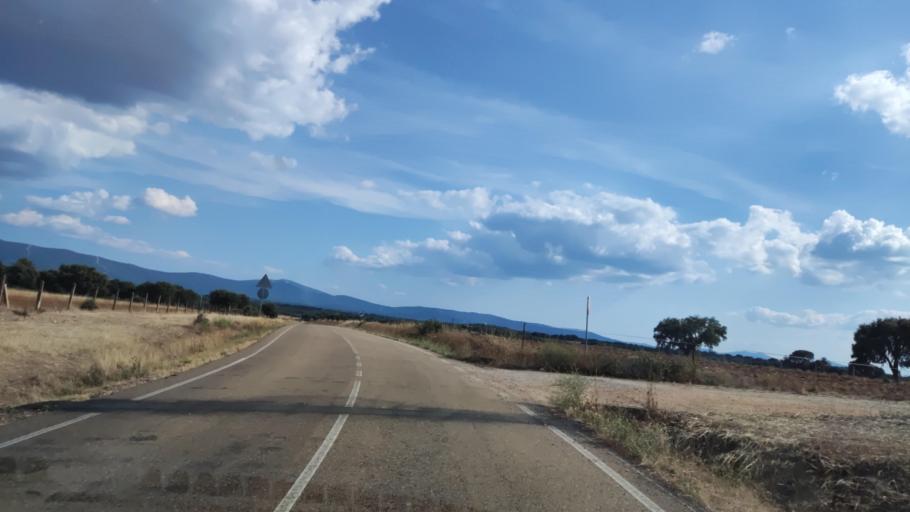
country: ES
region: Castille and Leon
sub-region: Provincia de Salamanca
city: Martiago
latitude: 40.4848
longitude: -6.4939
